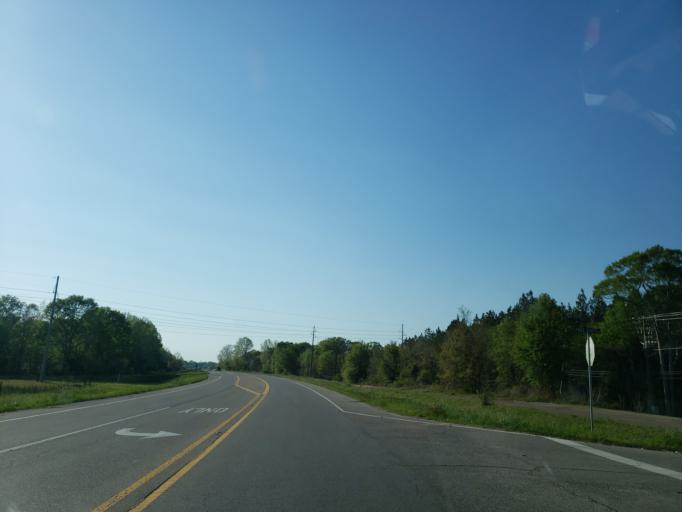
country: US
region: Mississippi
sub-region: Jones County
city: Laurel
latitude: 31.6788
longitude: -89.1116
